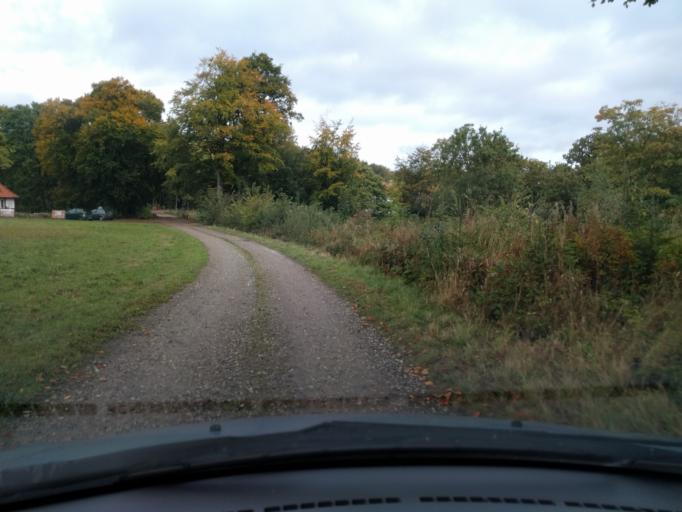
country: DK
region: South Denmark
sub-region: Kerteminde Kommune
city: Kerteminde
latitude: 55.4765
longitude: 10.6943
